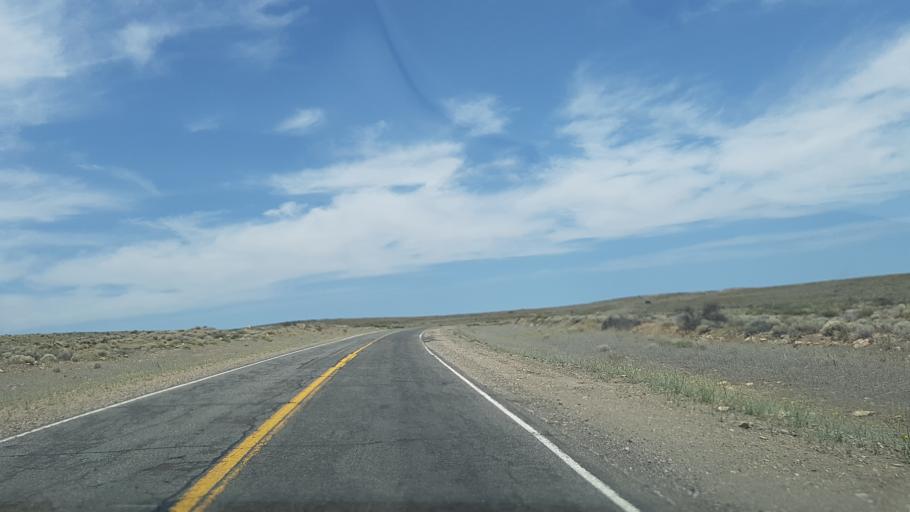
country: AR
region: Rio Negro
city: Pilcaniyeu
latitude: -40.4935
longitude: -70.6783
